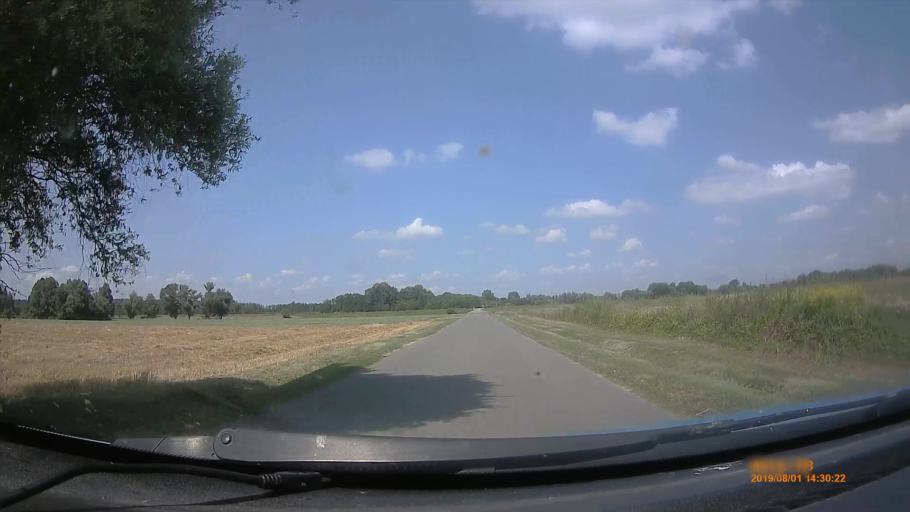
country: HR
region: Osjecko-Baranjska
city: Viljevo
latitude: 45.8029
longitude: 18.1003
